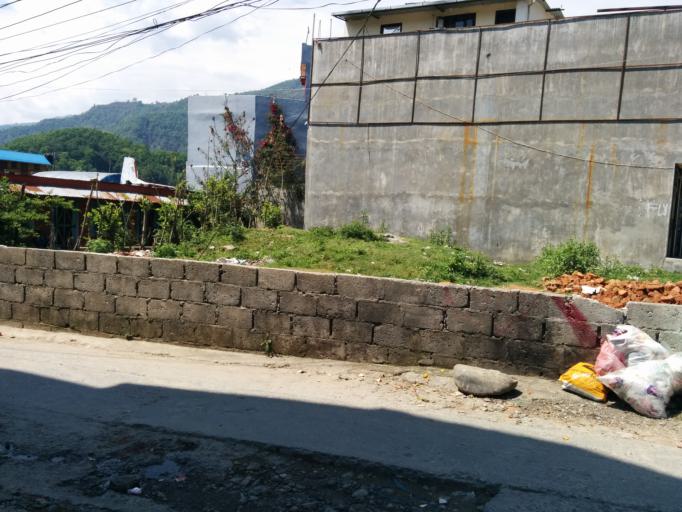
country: NP
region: Western Region
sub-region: Gandaki Zone
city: Pokhara
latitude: 28.2170
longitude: 83.9587
